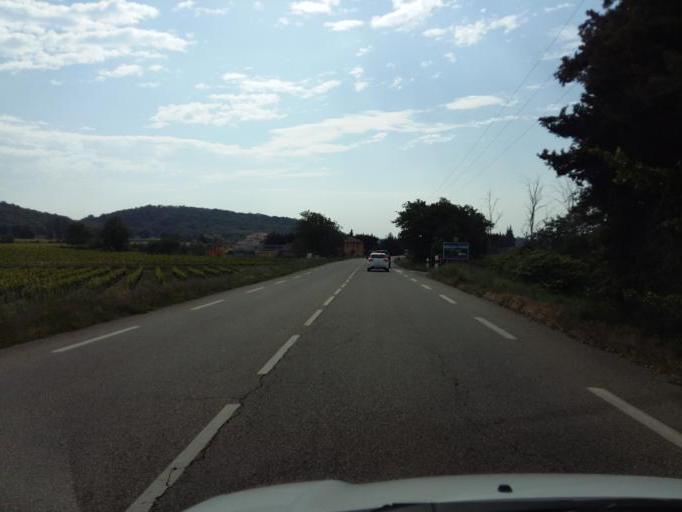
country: FR
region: Provence-Alpes-Cote d'Azur
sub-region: Departement du Vaucluse
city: Bollene
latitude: 44.2805
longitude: 4.7947
